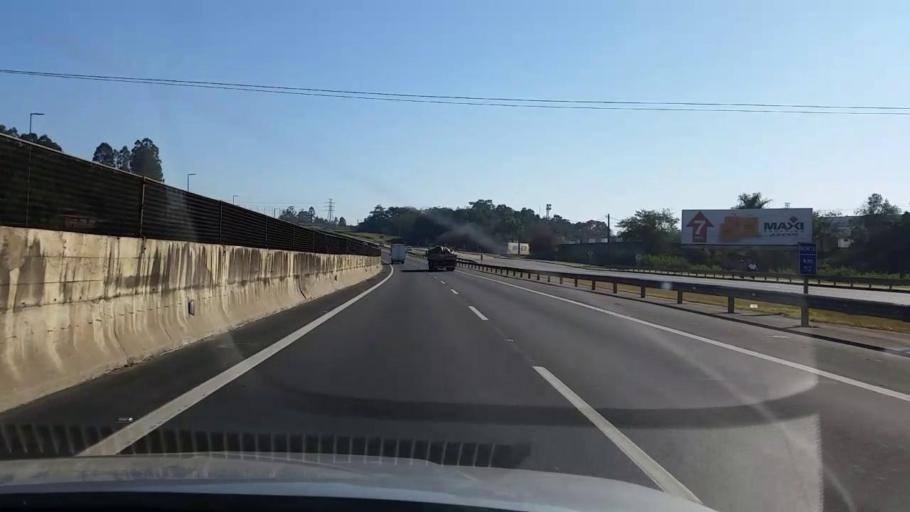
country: BR
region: Sao Paulo
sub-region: Varzea Paulista
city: Varzea Paulista
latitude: -23.2401
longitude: -46.8691
